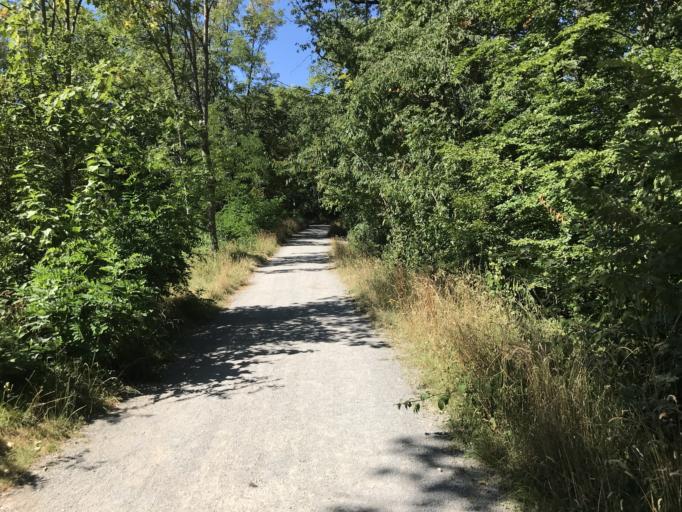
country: DE
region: Baden-Wuerttemberg
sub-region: Regierungsbezirk Stuttgart
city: Stuttgart
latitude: 48.7532
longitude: 9.1569
